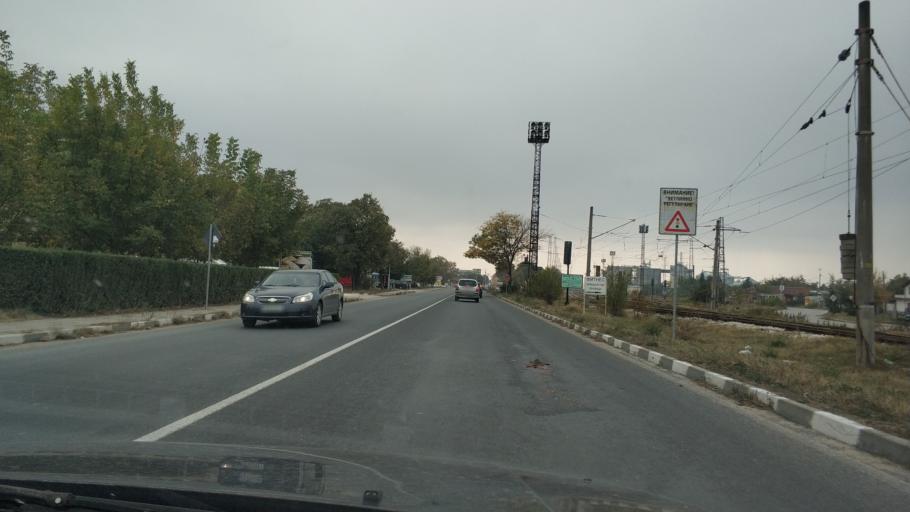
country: BG
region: Plovdiv
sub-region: Obshtina Plovdiv
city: Plovdiv
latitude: 42.2337
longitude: 24.7236
